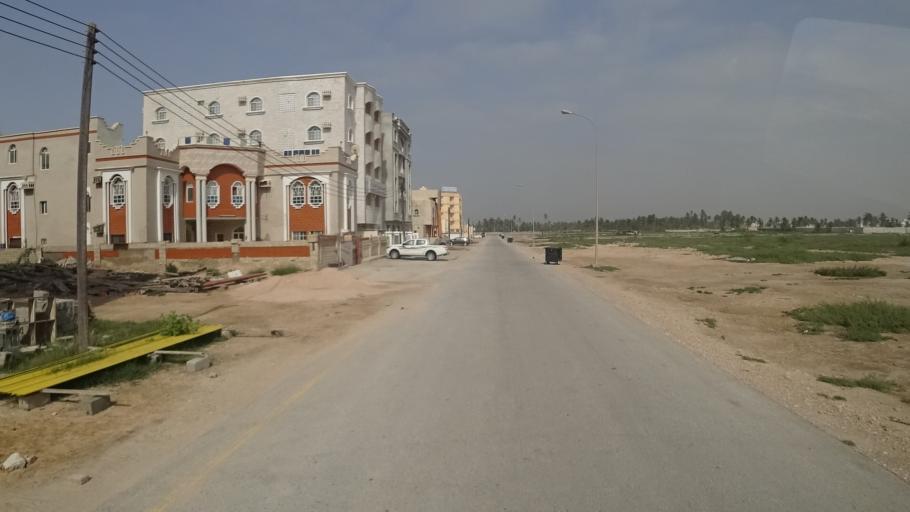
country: OM
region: Zufar
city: Salalah
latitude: 17.0163
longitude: 54.1741
